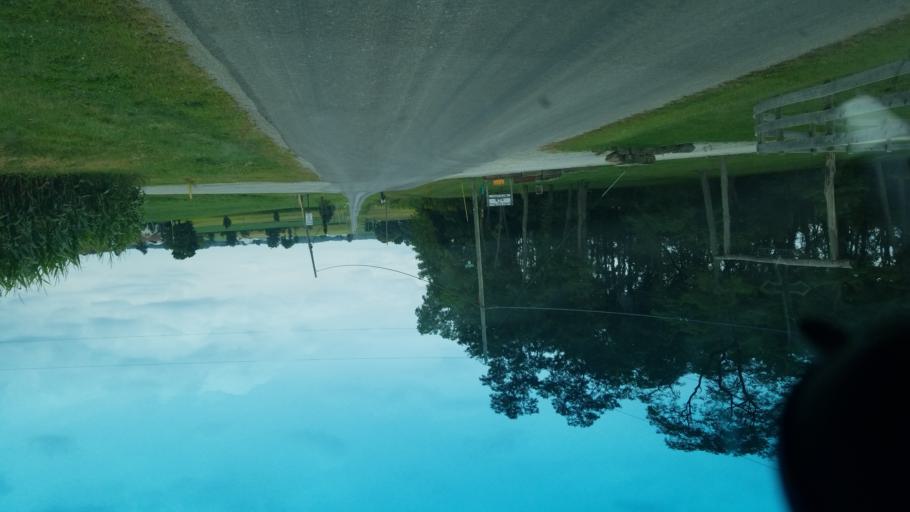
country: US
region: Ohio
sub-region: Richland County
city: Shelby
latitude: 40.9381
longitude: -82.5985
